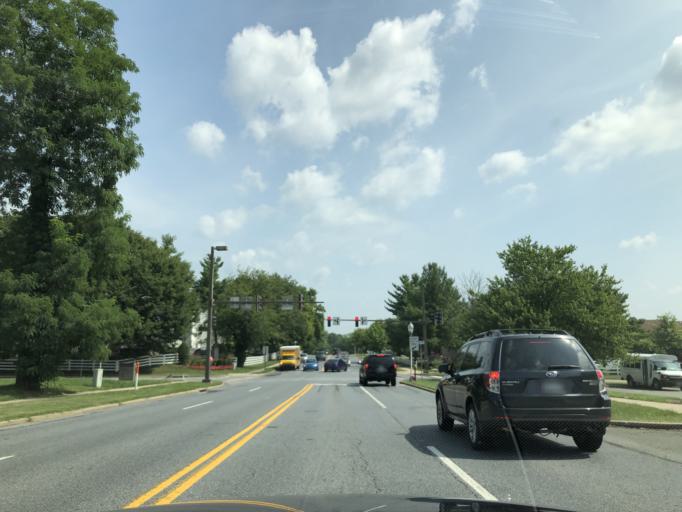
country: US
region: Maryland
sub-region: Frederick County
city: Frederick
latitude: 39.4207
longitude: -77.4496
